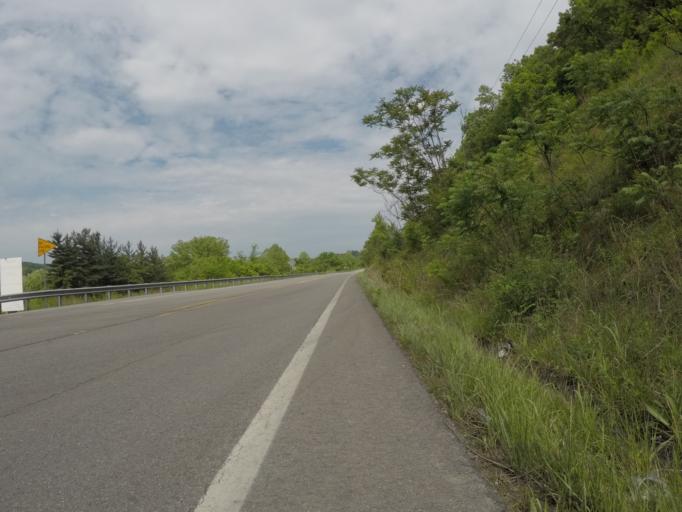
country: US
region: West Virginia
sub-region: Wayne County
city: Kenova
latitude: 38.3398
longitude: -82.5849
